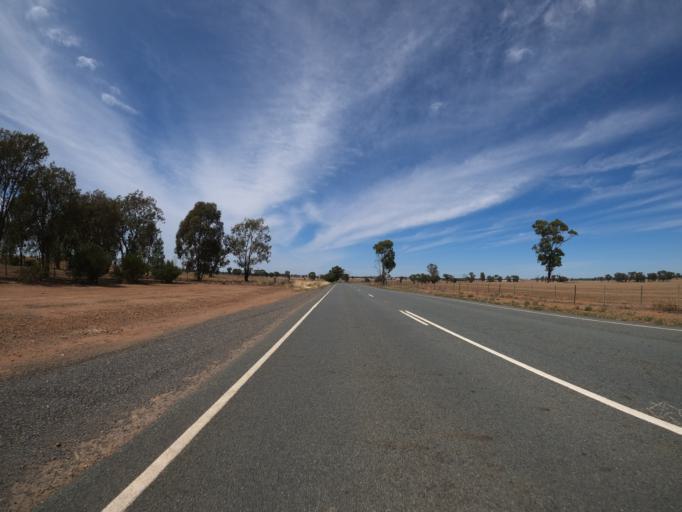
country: AU
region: Victoria
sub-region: Moira
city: Yarrawonga
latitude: -36.0494
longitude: 145.9955
